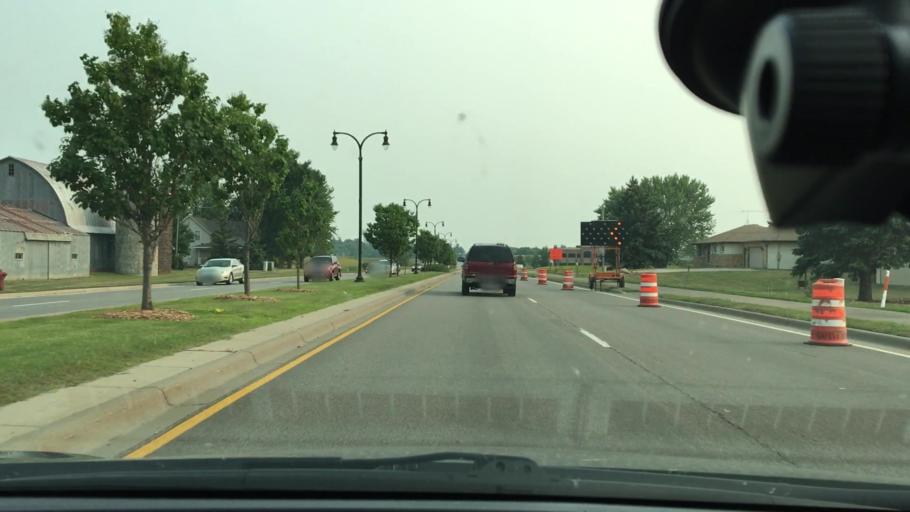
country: US
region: Minnesota
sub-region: Wright County
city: Albertville
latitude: 45.2321
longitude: -93.6644
